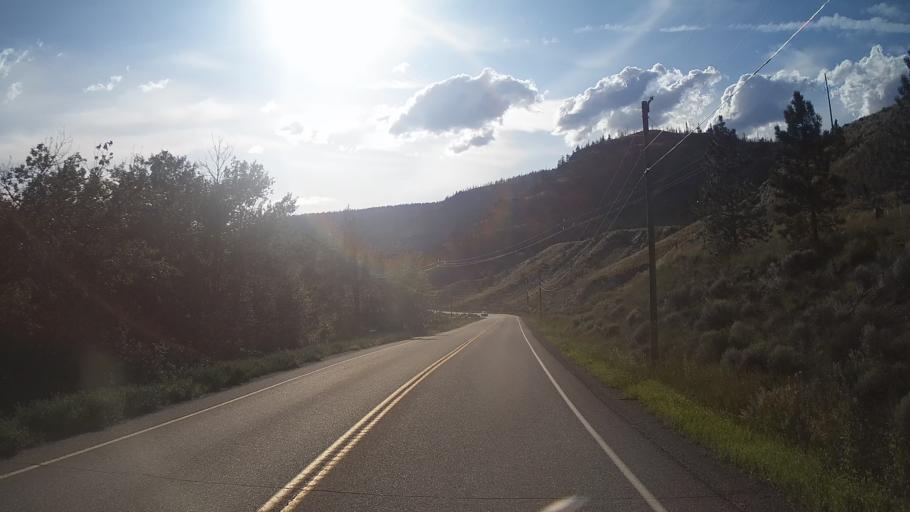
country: CA
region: British Columbia
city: Cache Creek
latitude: 50.8843
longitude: -121.4768
